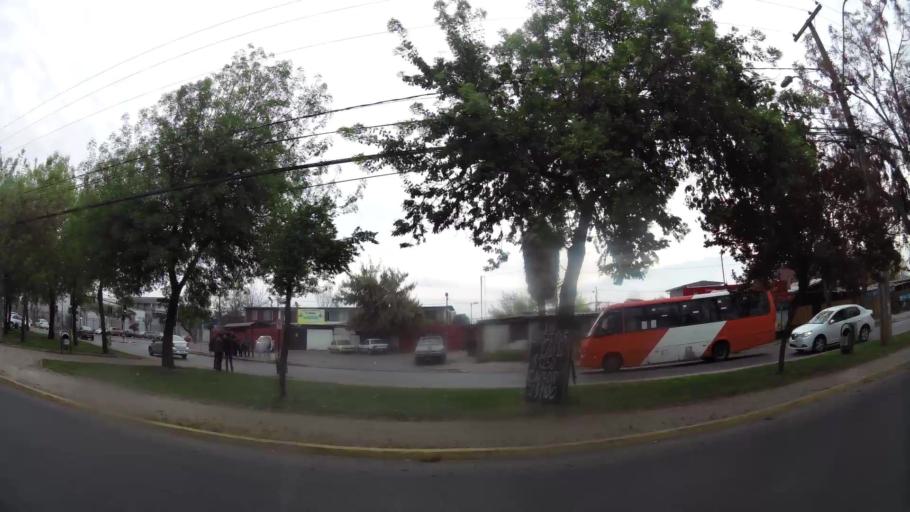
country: CL
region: Santiago Metropolitan
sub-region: Provincia de Santiago
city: Villa Presidente Frei, Nunoa, Santiago, Chile
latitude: -33.4701
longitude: -70.6138
